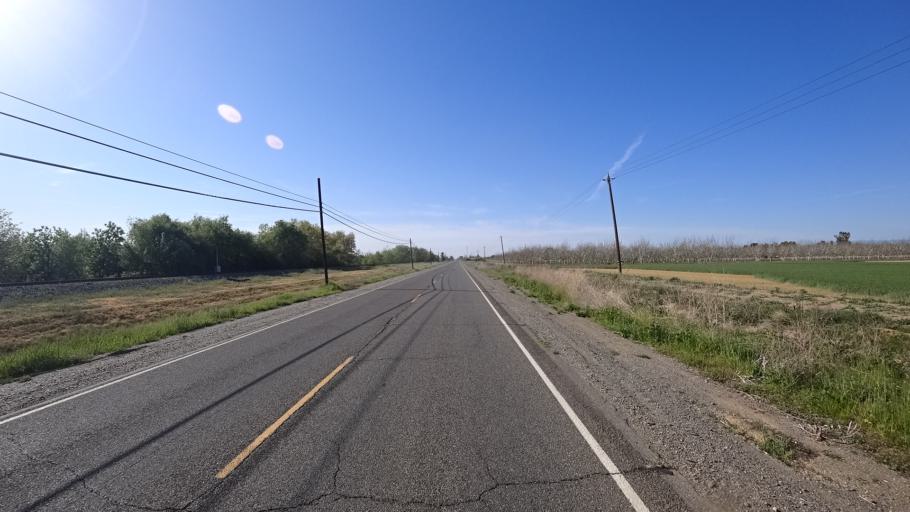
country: US
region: California
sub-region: Glenn County
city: Willows
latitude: 39.5471
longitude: -122.1936
